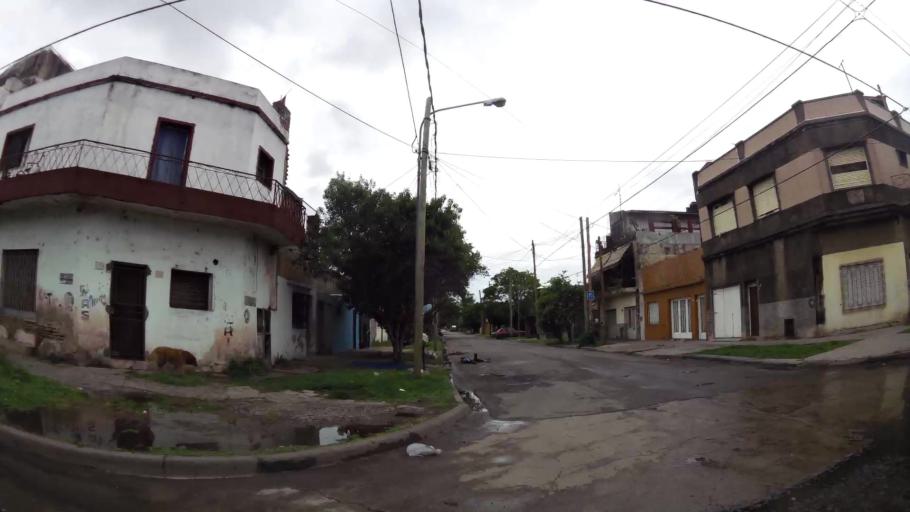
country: AR
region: Buenos Aires
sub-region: Partido de Lanus
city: Lanus
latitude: -34.7282
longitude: -58.3677
